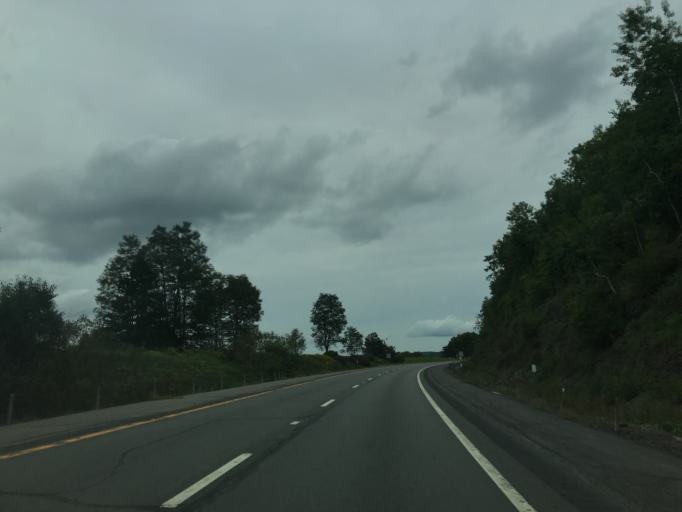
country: US
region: New York
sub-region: Chenango County
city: Bainbridge
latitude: 42.2942
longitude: -75.4610
